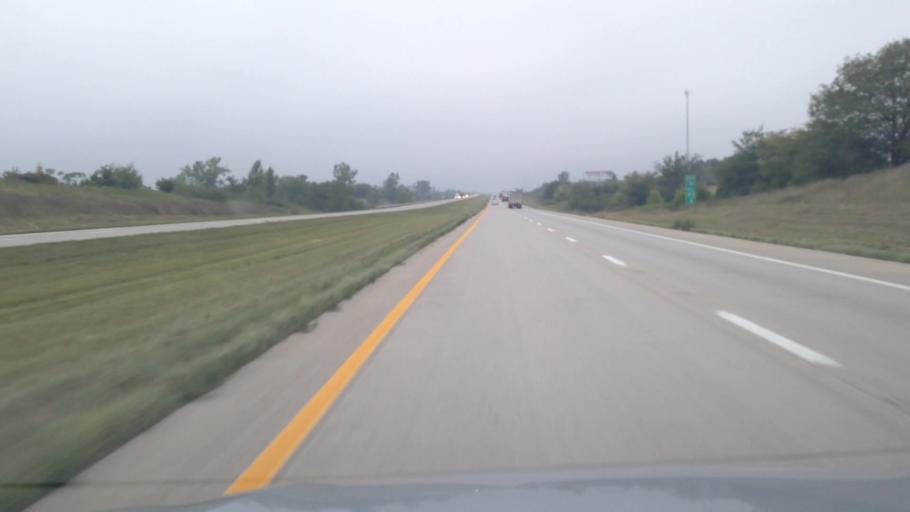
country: US
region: Missouri
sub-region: Clinton County
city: Lathrop
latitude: 39.6054
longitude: -94.2524
